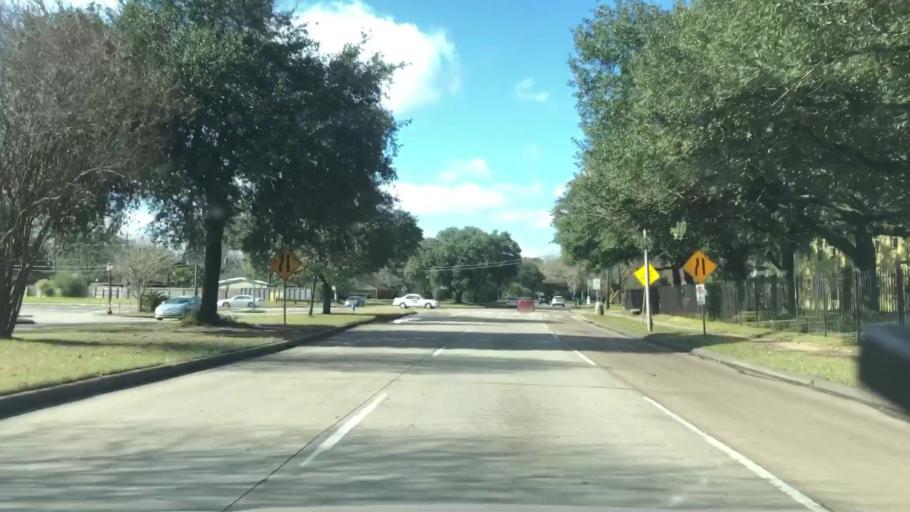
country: US
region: Texas
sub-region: Harris County
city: Bellaire
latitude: 29.6579
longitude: -95.4806
